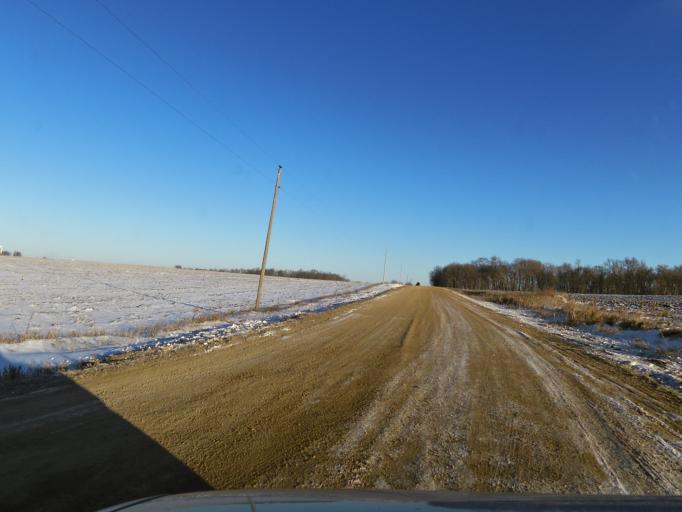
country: US
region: Minnesota
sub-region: Scott County
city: Jordan
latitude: 44.6633
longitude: -93.5422
